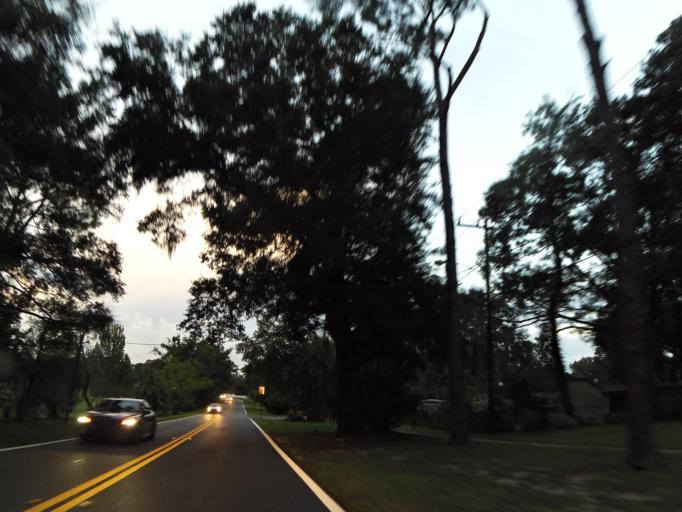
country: US
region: Florida
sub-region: Duval County
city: Jacksonville
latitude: 30.3743
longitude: -81.6073
